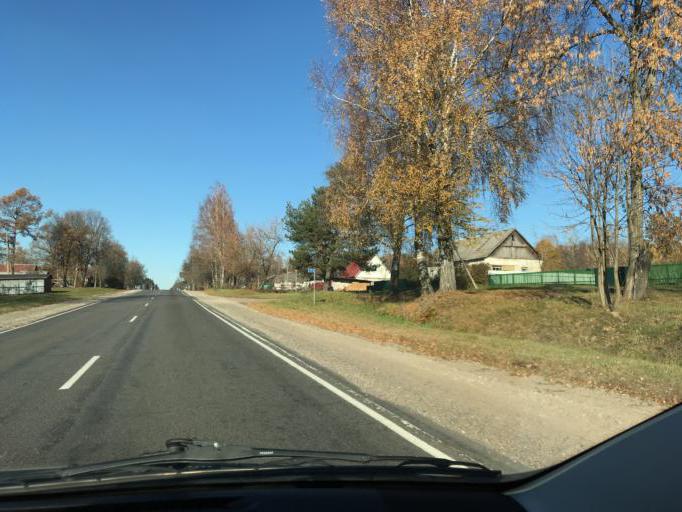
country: BY
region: Vitebsk
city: Polatsk
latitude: 55.5344
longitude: 28.7195
